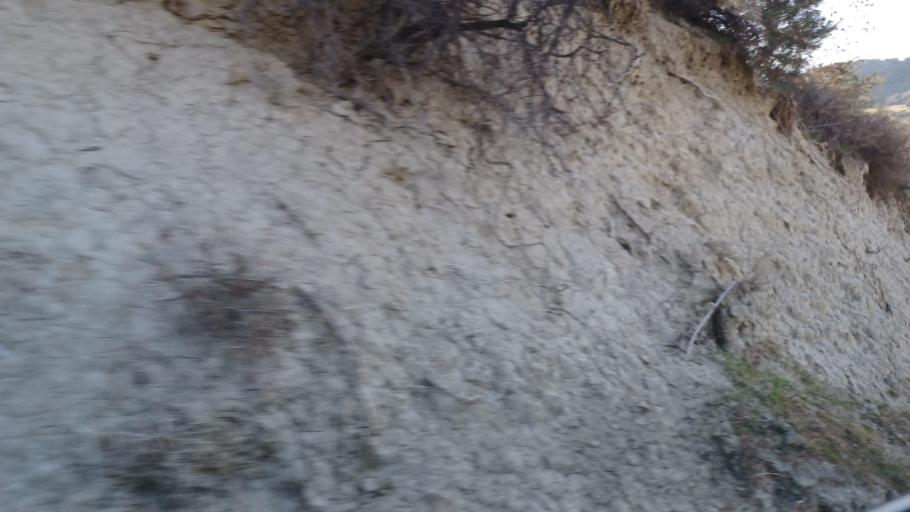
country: CY
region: Pafos
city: Polis
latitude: 34.9972
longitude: 32.4585
